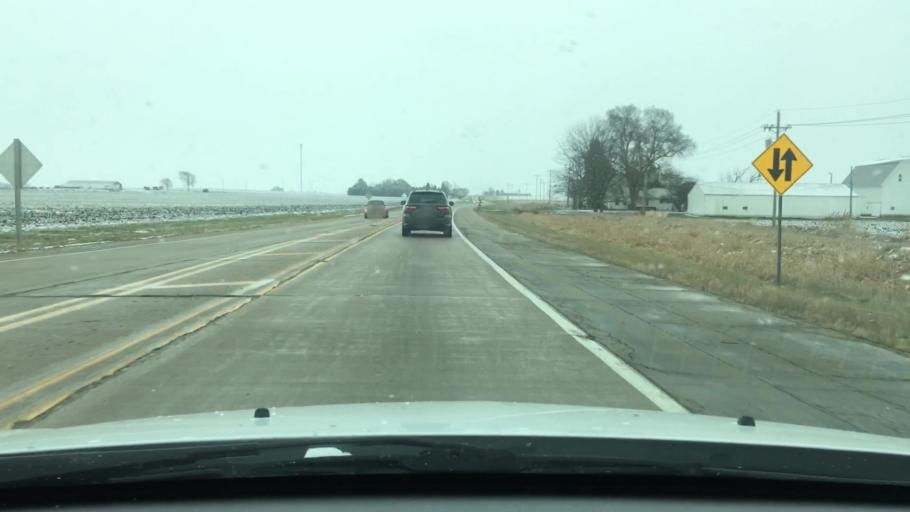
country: US
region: Illinois
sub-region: Ogle County
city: Hillcrest
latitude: 41.9347
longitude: -89.0186
